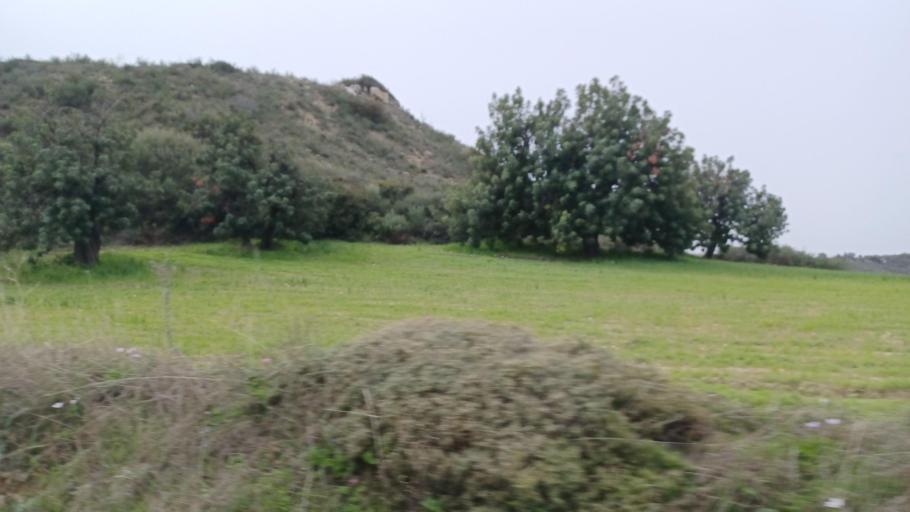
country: CY
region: Limassol
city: Pissouri
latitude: 34.7197
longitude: 32.7387
